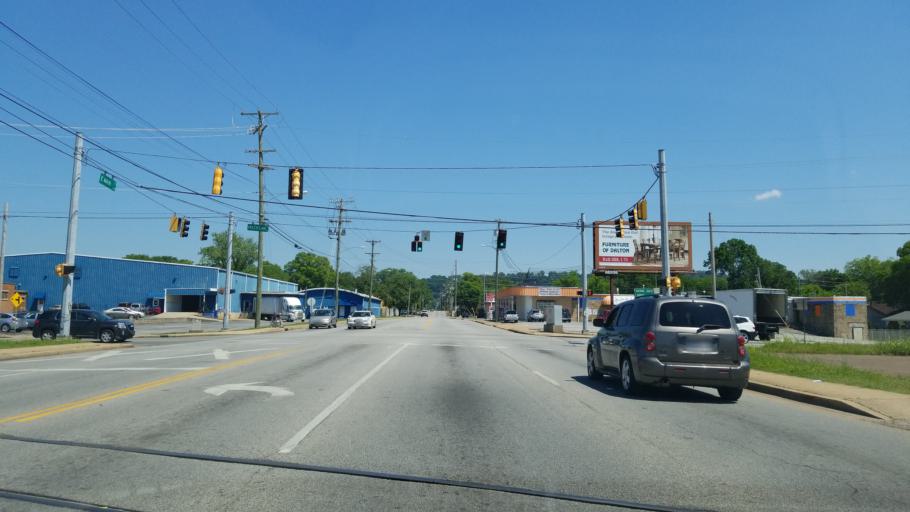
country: US
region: Tennessee
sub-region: Hamilton County
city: Chattanooga
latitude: 35.0291
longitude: -85.2886
